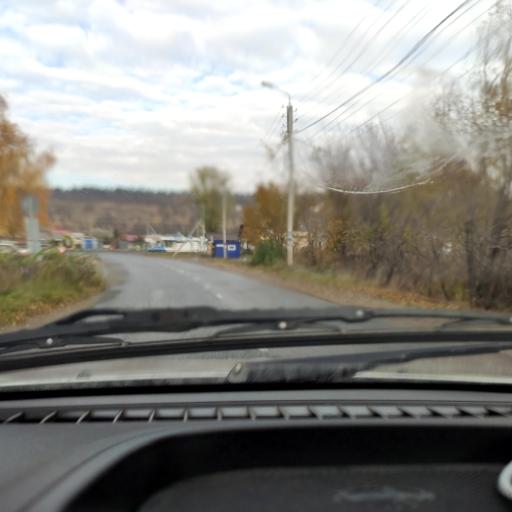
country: RU
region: Samara
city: Zhigulevsk
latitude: 53.4655
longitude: 49.6207
